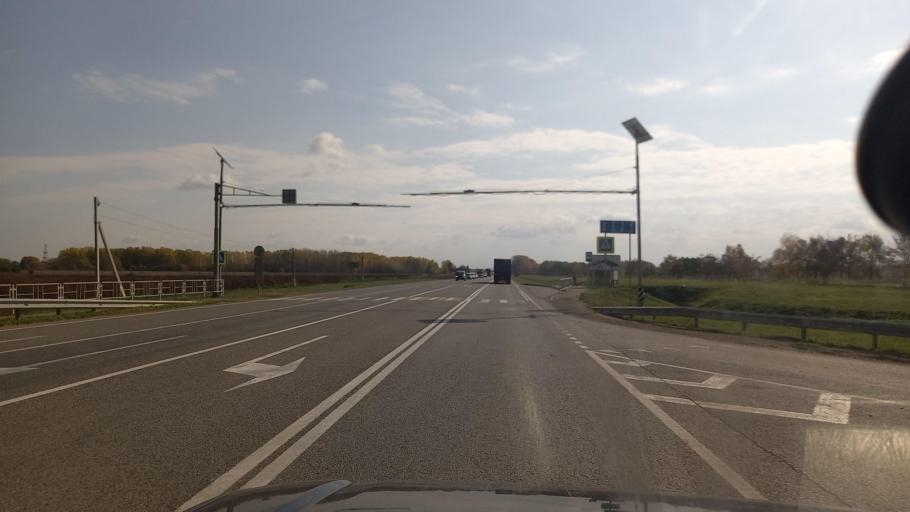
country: RU
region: Krasnodarskiy
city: Novoukrainskiy
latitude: 44.8893
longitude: 38.0751
